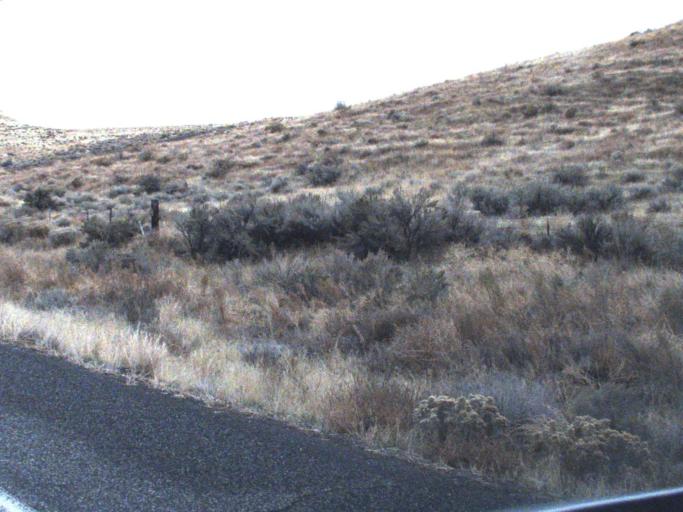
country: US
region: Washington
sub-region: Benton County
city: Finley
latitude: 46.0695
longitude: -118.8127
